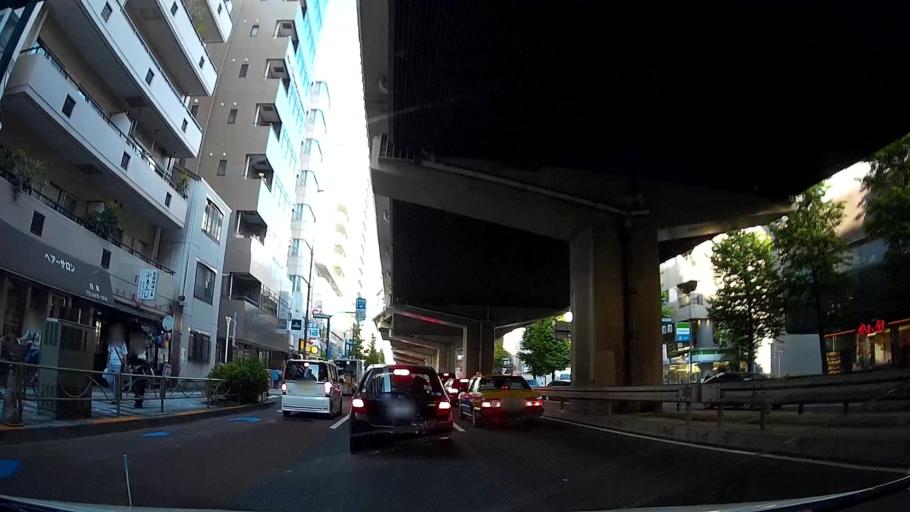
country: JP
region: Tokyo
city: Tokyo
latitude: 35.6319
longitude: 139.6586
